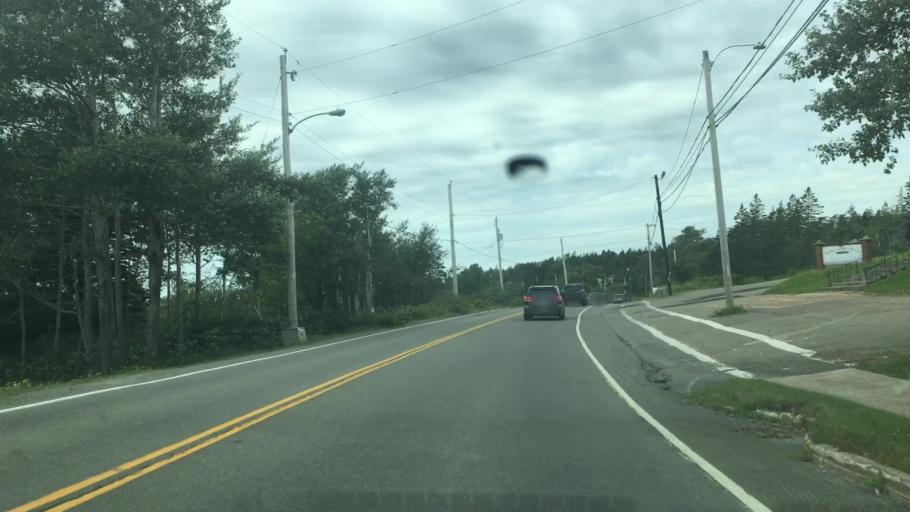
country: CA
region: Nova Scotia
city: Princeville
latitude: 45.6557
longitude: -60.8835
